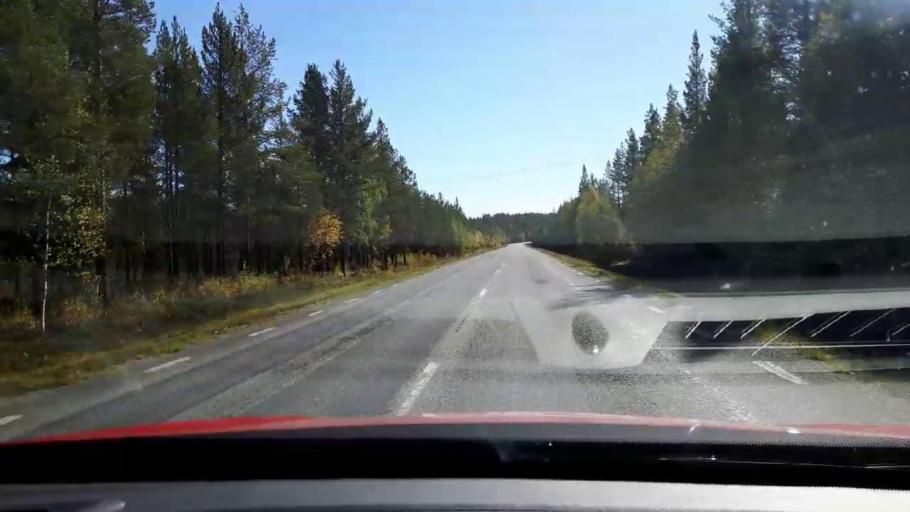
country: SE
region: Jaemtland
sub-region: Harjedalens Kommun
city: Sveg
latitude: 62.3371
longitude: 14.0463
